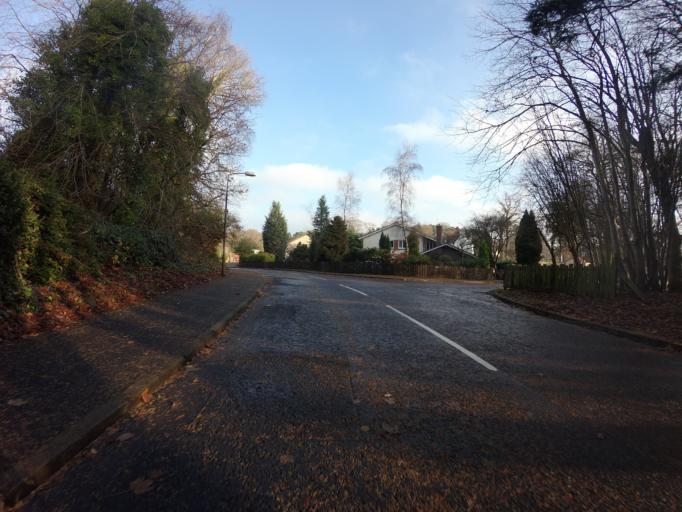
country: GB
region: Scotland
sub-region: West Lothian
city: Livingston
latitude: 55.9090
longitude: -3.5582
